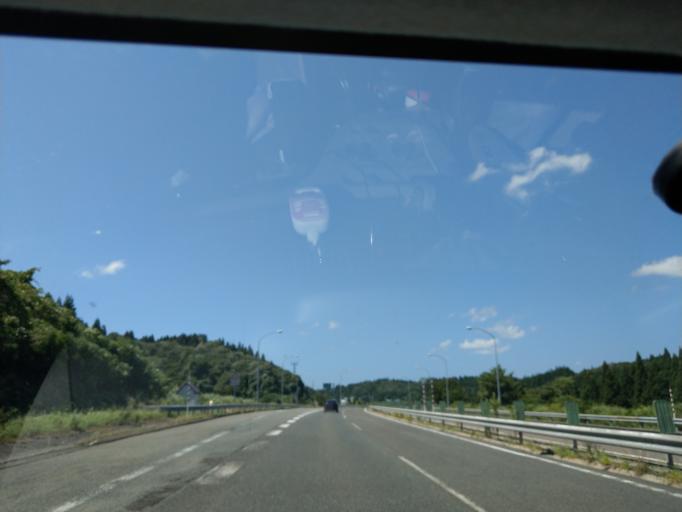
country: JP
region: Akita
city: Akita
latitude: 39.6573
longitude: 140.1949
